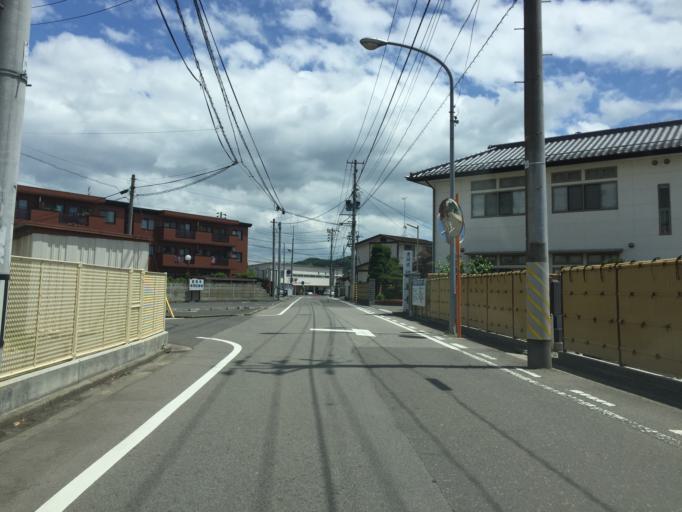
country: JP
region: Fukushima
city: Fukushima-shi
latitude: 37.7557
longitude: 140.4785
